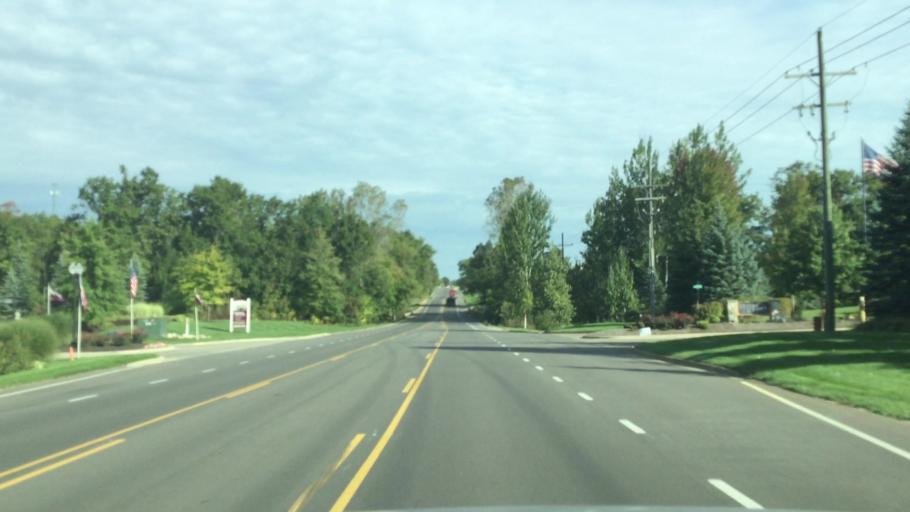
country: US
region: Michigan
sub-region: Livingston County
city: Howell
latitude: 42.6179
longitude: -83.8751
